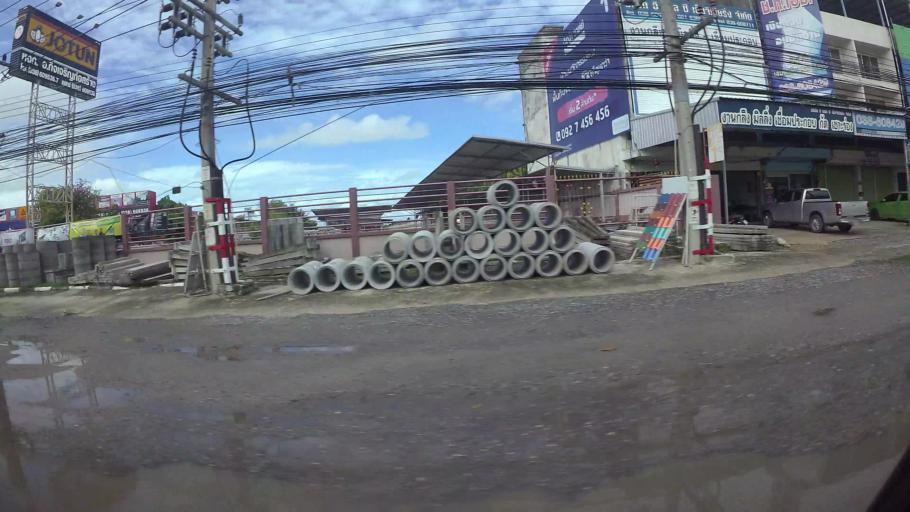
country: TH
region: Rayong
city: Rayong
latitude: 12.7089
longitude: 101.1756
